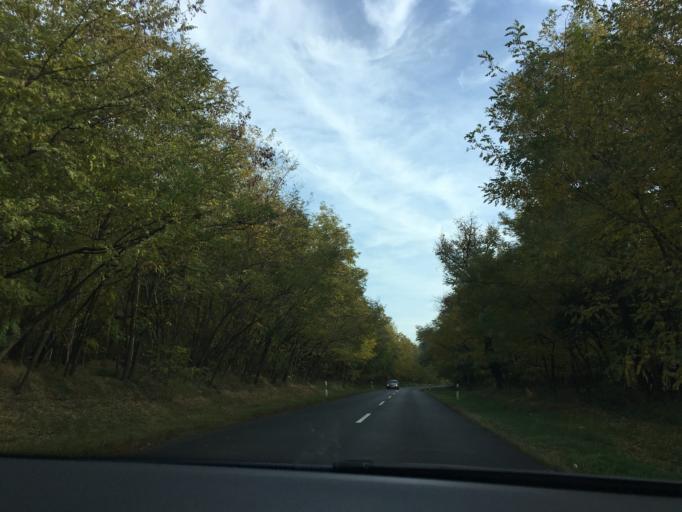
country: HU
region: Szabolcs-Szatmar-Bereg
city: Kisleta
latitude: 47.8517
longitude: 22.0290
